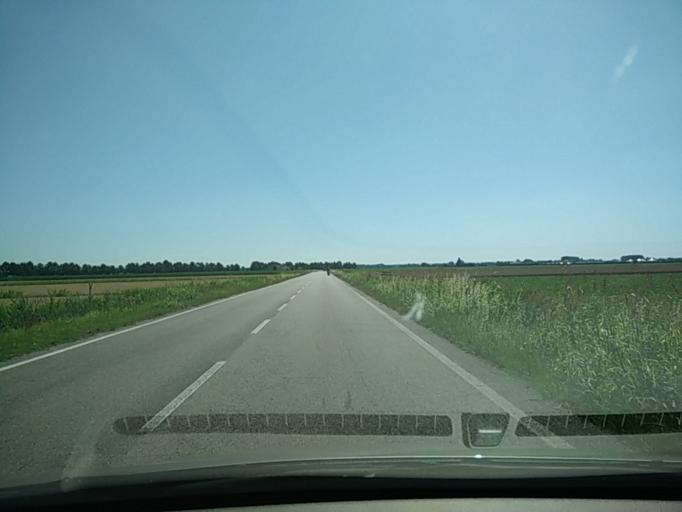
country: IT
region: Veneto
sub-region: Provincia di Venezia
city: San Giorgio di Livenza
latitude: 45.6353
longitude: 12.7557
